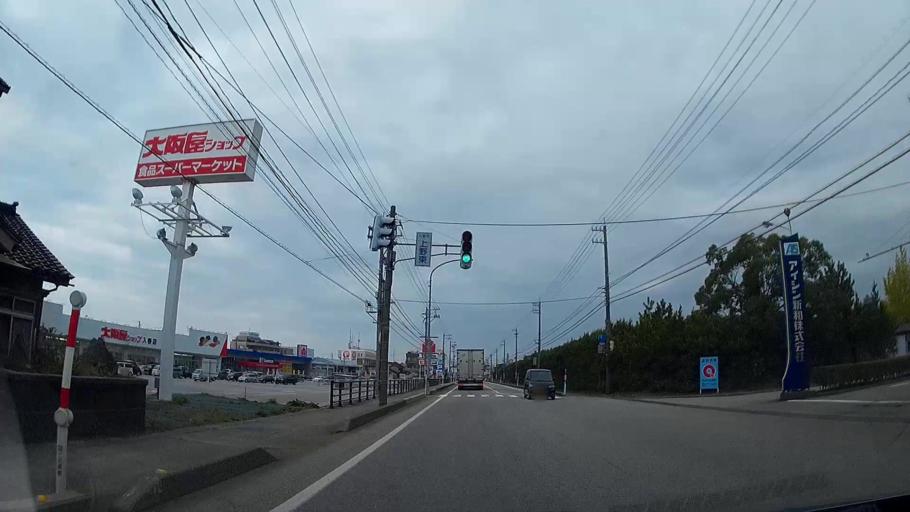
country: JP
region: Toyama
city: Nyuzen
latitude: 36.9307
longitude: 137.4998
